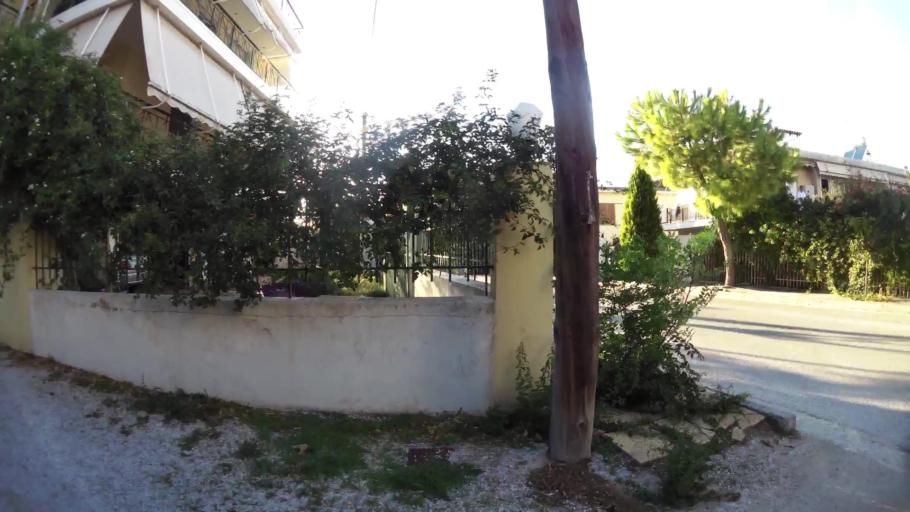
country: GR
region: Attica
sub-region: Nomarchia Anatolikis Attikis
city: Rafina
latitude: 38.0215
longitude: 24.0010
